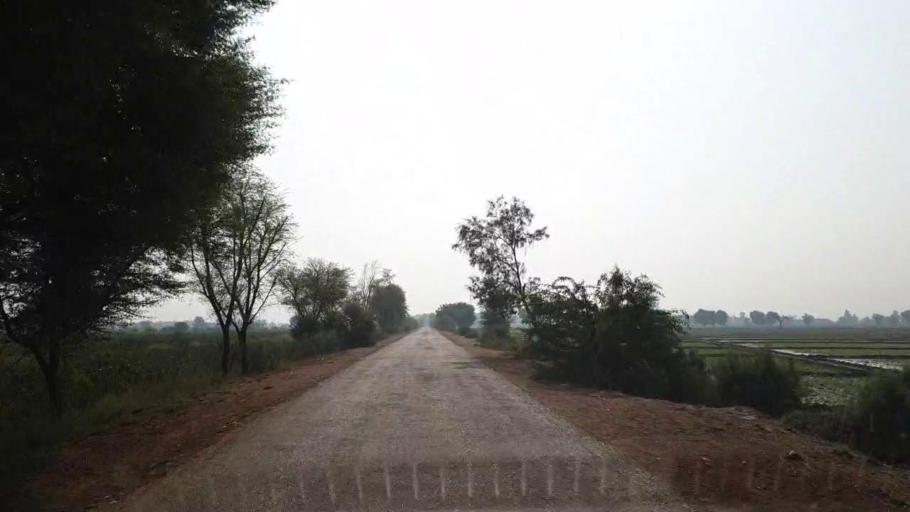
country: PK
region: Sindh
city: Sehwan
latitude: 26.4720
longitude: 67.7749
